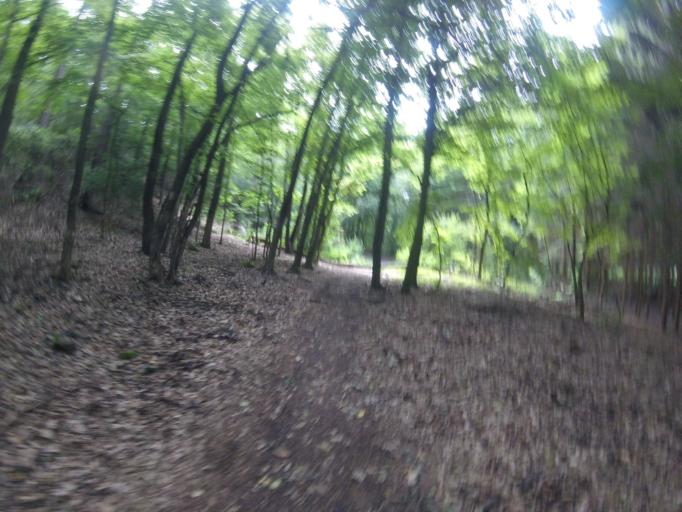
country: HU
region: Nograd
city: Tar
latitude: 47.9466
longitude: 19.7677
